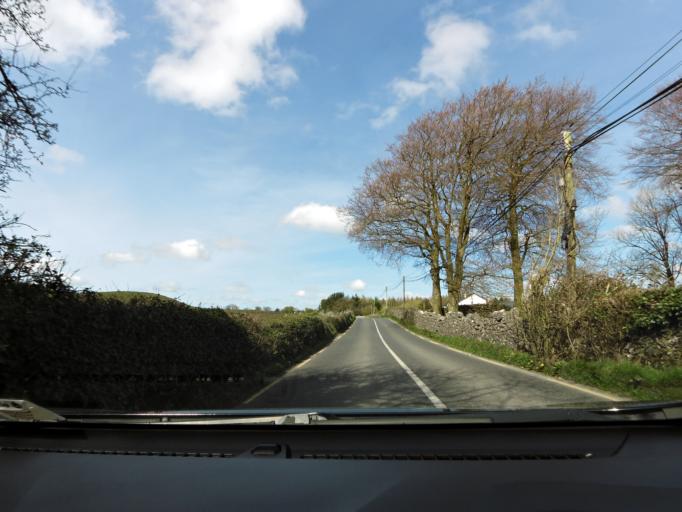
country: IE
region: Connaught
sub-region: County Galway
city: Athenry
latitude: 53.3047
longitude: -8.7697
